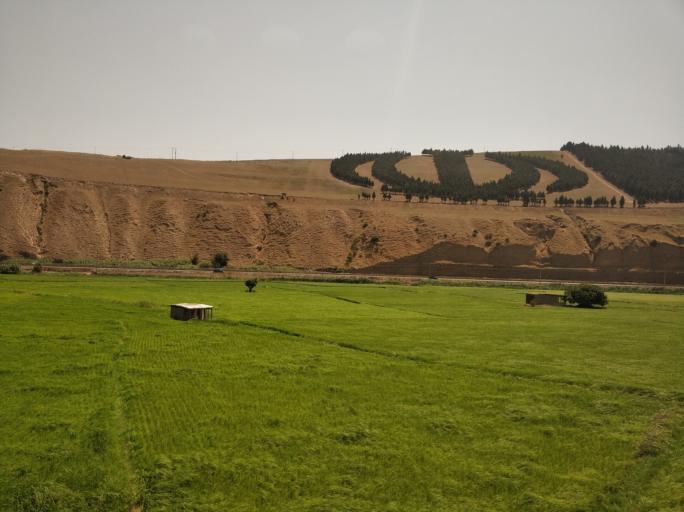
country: IR
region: Gilan
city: Pa'in-e Bazar-e Rudbar
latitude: 36.9157
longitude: 49.5212
